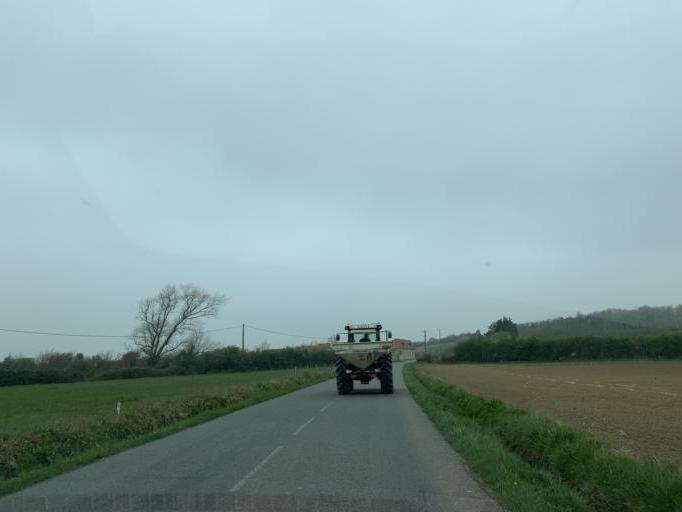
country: FR
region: Nord-Pas-de-Calais
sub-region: Departement du Pas-de-Calais
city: Marquise
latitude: 50.7945
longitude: 1.7137
